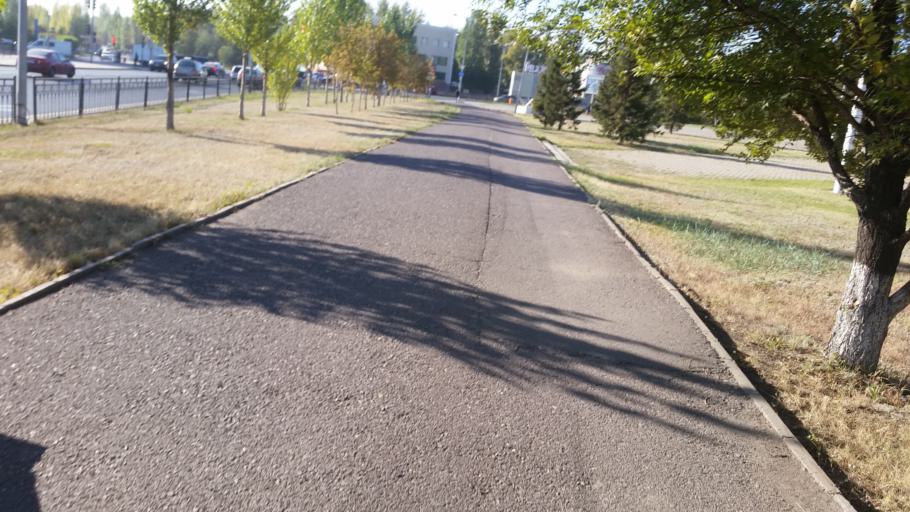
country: KZ
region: Astana Qalasy
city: Astana
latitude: 51.1552
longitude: 71.4666
